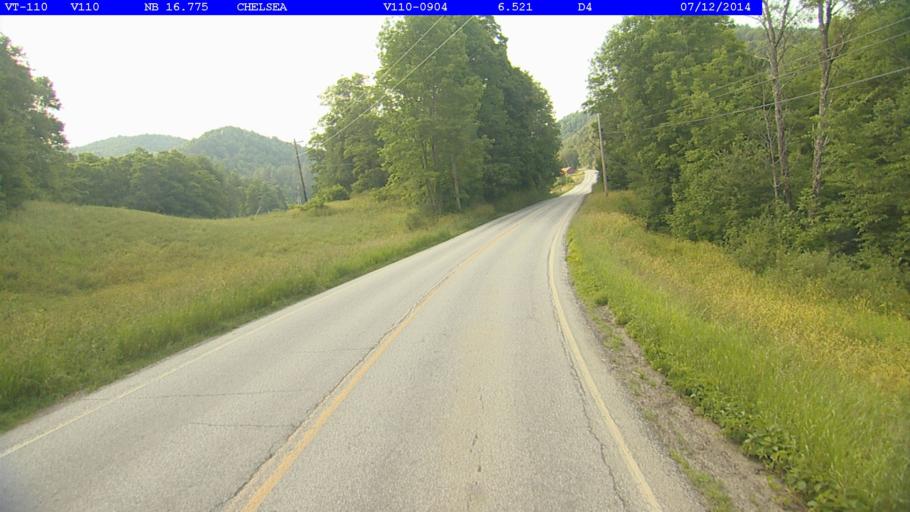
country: US
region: Vermont
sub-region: Orange County
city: Chelsea
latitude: 44.0344
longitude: -72.4751
